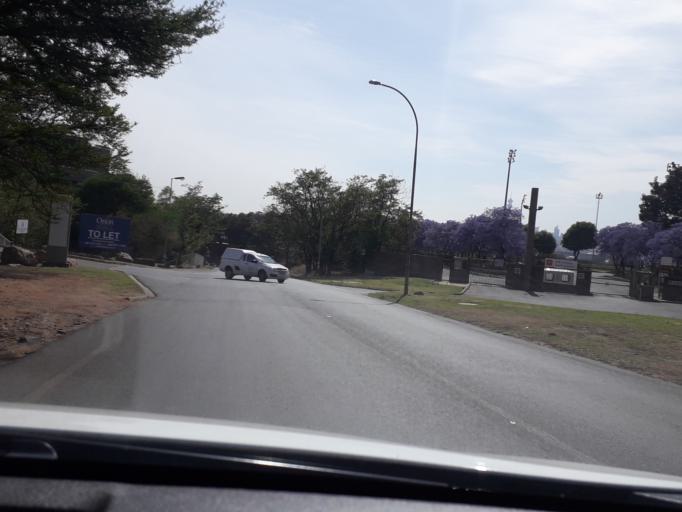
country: ZA
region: Gauteng
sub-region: City of Johannesburg Metropolitan Municipality
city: Johannesburg
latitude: -26.1914
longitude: 28.0074
